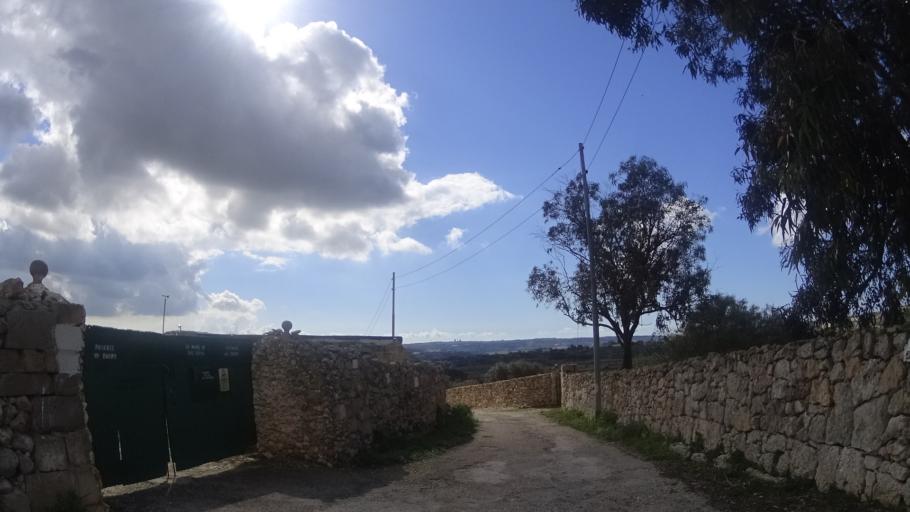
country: MT
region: L-Imtarfa
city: Imtarfa
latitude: 35.9057
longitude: 14.3841
